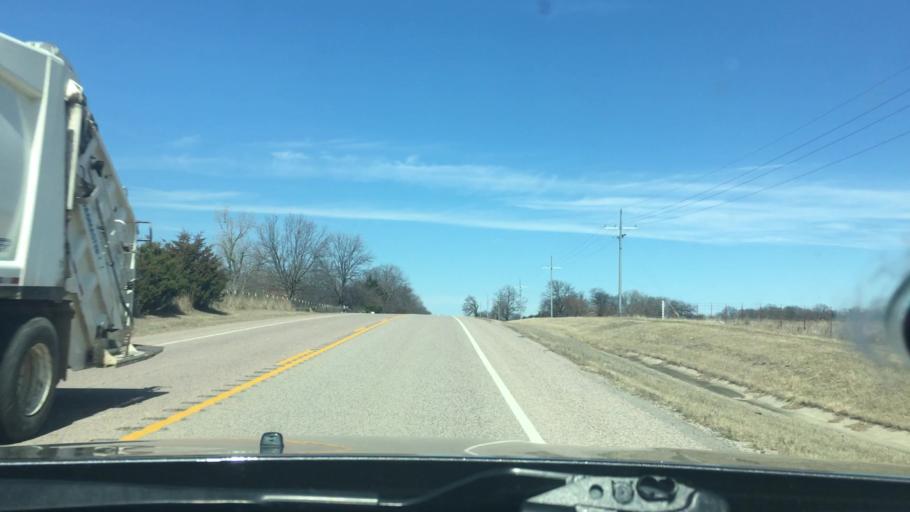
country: US
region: Oklahoma
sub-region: Murray County
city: Sulphur
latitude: 34.4136
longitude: -96.9508
